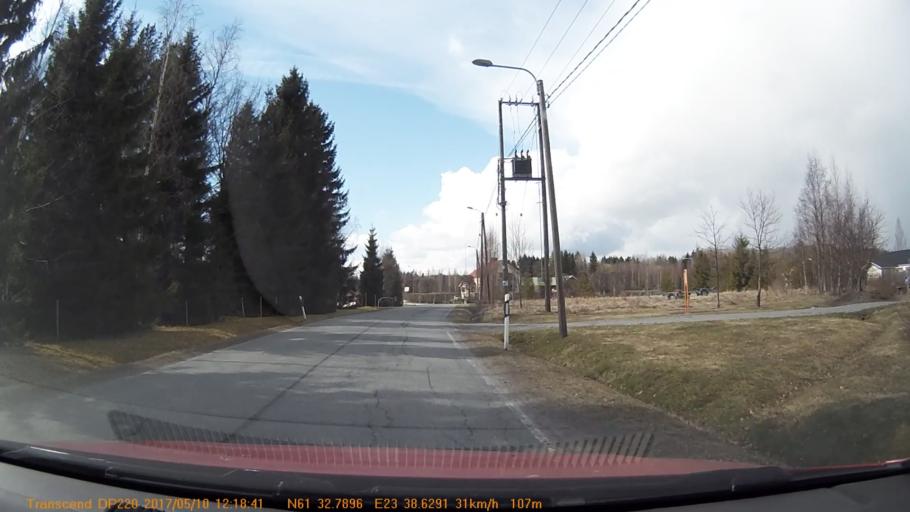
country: FI
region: Pirkanmaa
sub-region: Tampere
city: Yloejaervi
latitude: 61.5465
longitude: 23.6439
